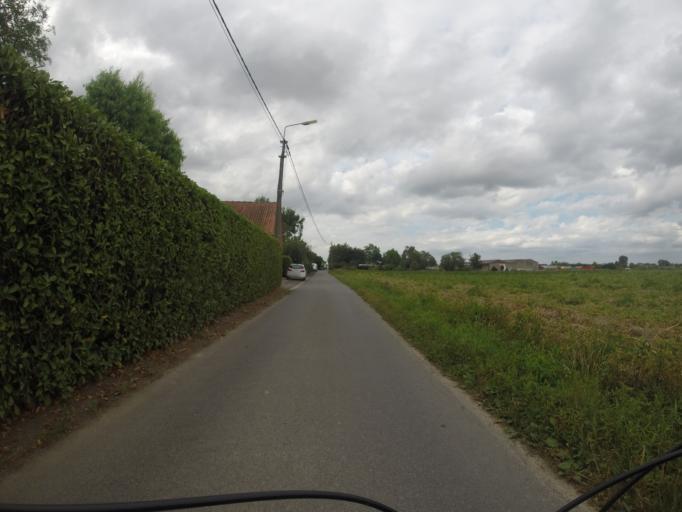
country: BE
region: Flanders
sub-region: Provincie West-Vlaanderen
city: Hooglede
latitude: 50.9469
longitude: 3.0790
